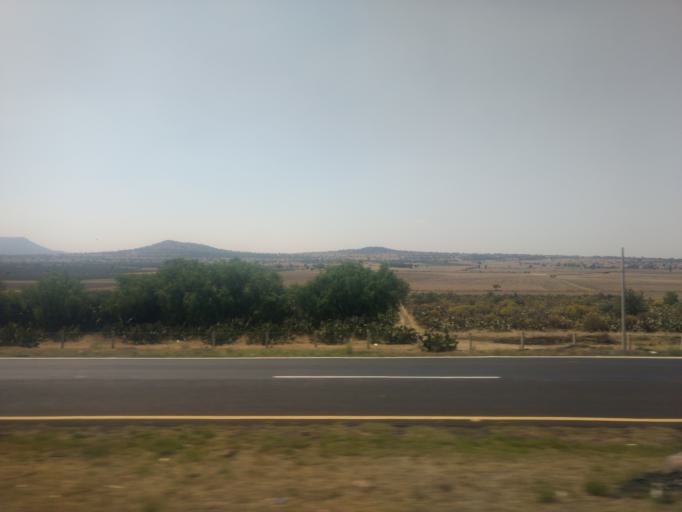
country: MX
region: Morelos
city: Nopaltepec
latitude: 19.8025
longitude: -98.7242
